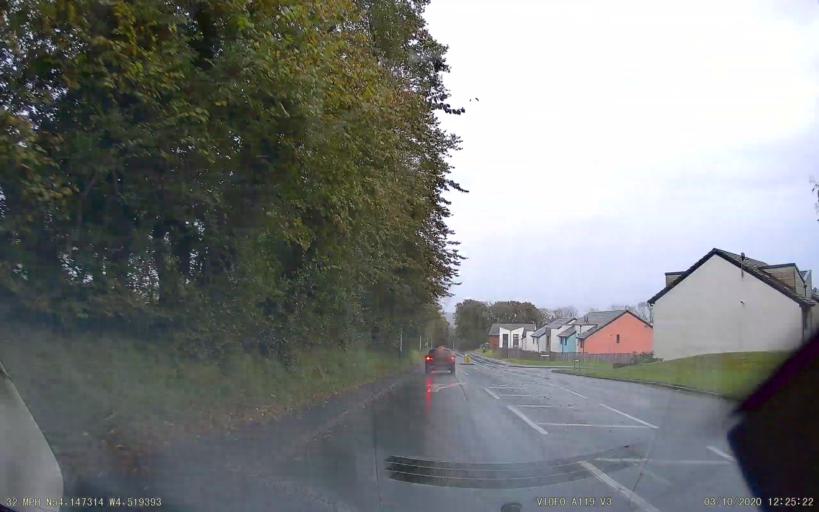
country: IM
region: Douglas
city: Douglas
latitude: 54.1473
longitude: -4.5194
